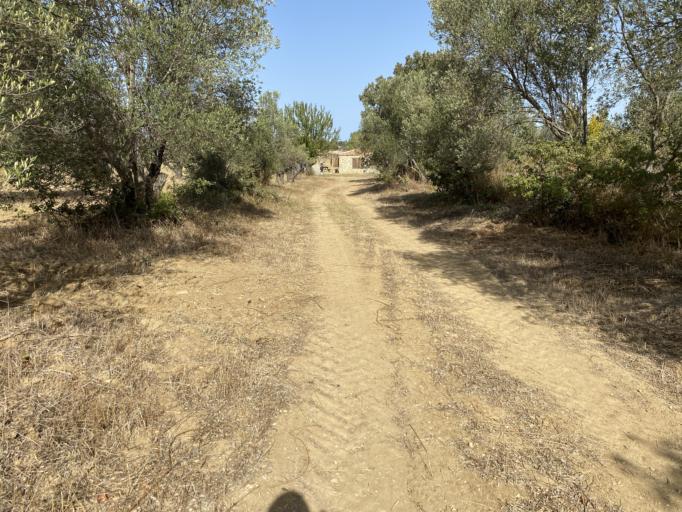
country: TR
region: Canakkale
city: Eceabat
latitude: 40.1819
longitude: 26.2871
